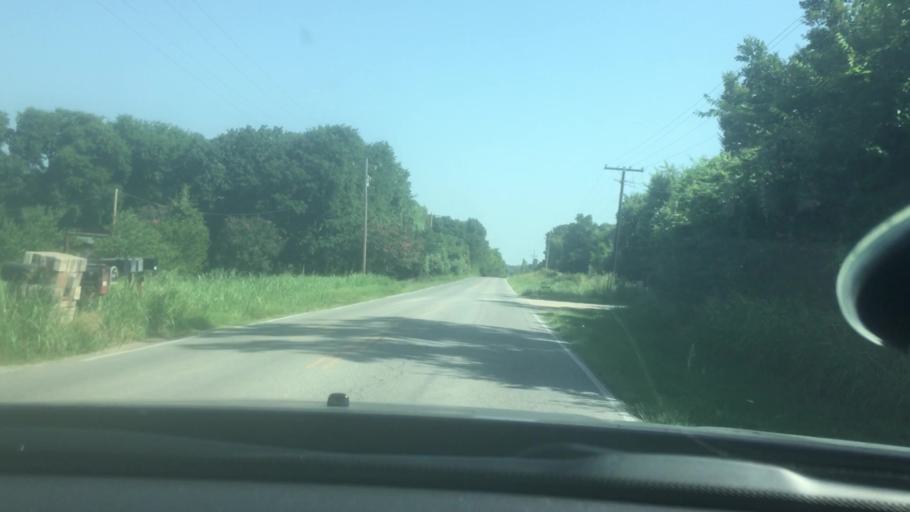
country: US
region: Oklahoma
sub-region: Bryan County
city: Calera
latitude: 34.0126
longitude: -96.4656
